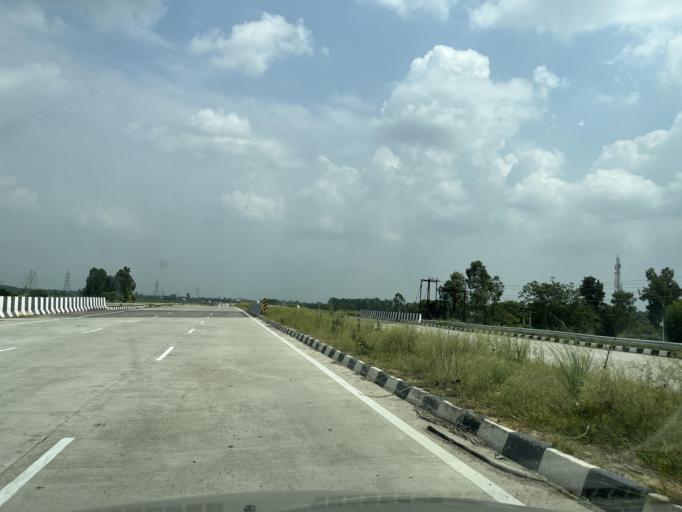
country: IN
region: Uttar Pradesh
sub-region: Bijnor
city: Dhampur
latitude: 29.3190
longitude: 78.5297
